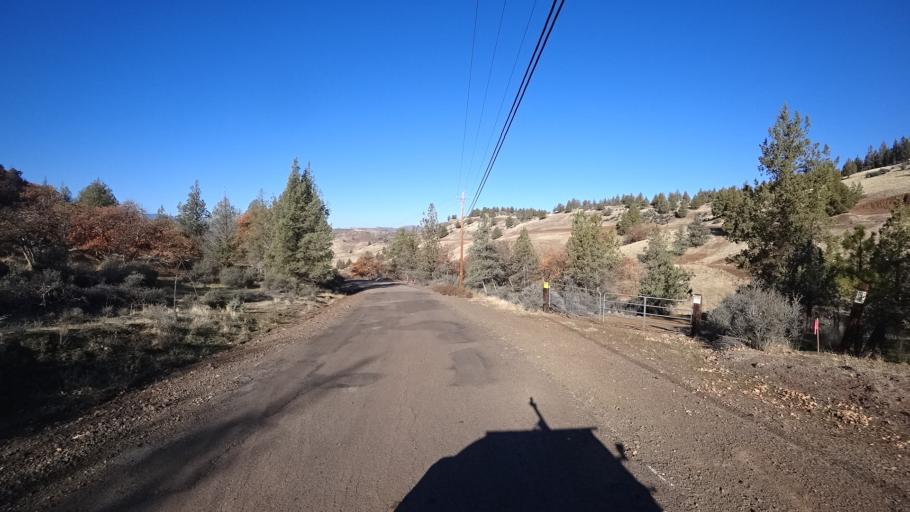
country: US
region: California
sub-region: Siskiyou County
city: Montague
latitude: 41.9146
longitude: -122.4343
